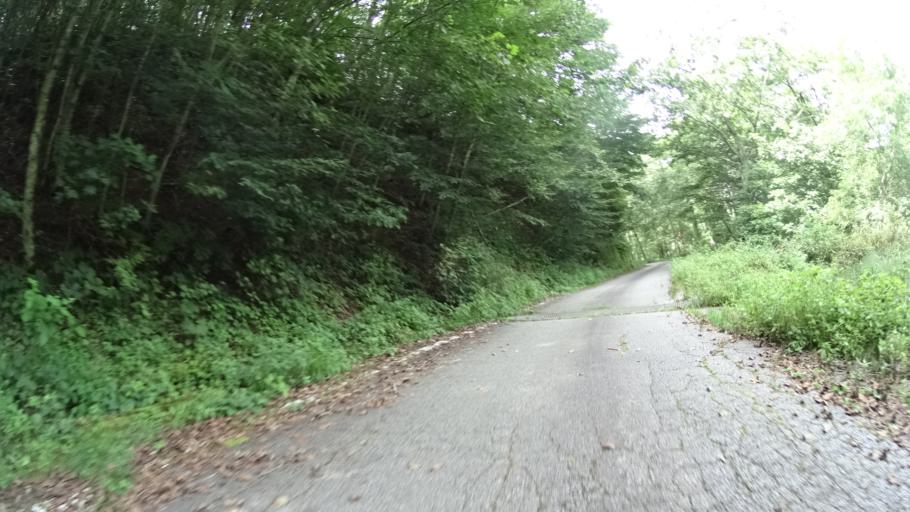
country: JP
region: Yamanashi
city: Nirasaki
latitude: 35.8037
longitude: 138.5438
